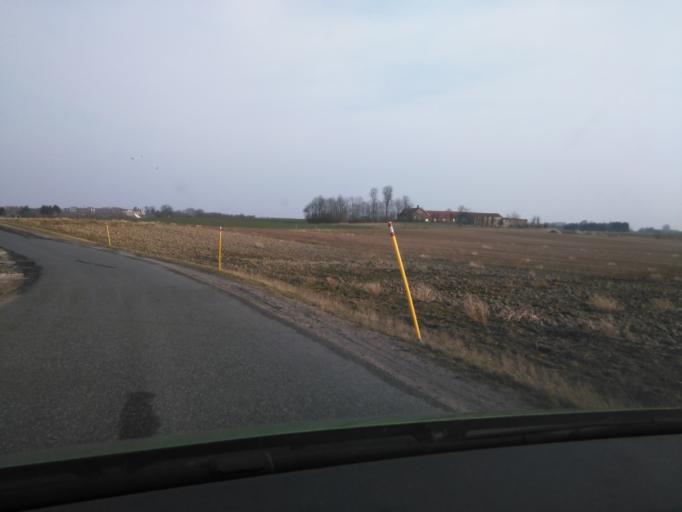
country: DK
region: Central Jutland
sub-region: Arhus Kommune
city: Marslet
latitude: 56.0914
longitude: 10.1539
